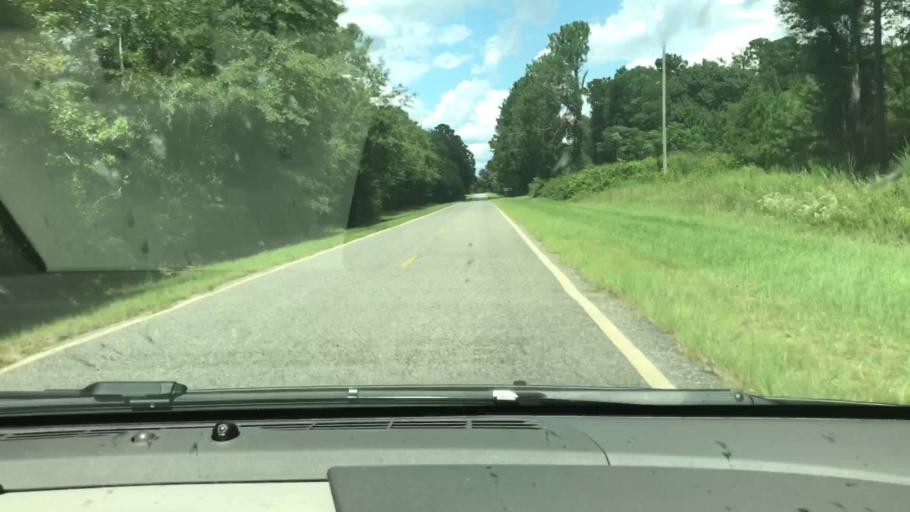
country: US
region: Georgia
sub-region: Clay County
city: Fort Gaines
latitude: 31.7438
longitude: -85.0827
